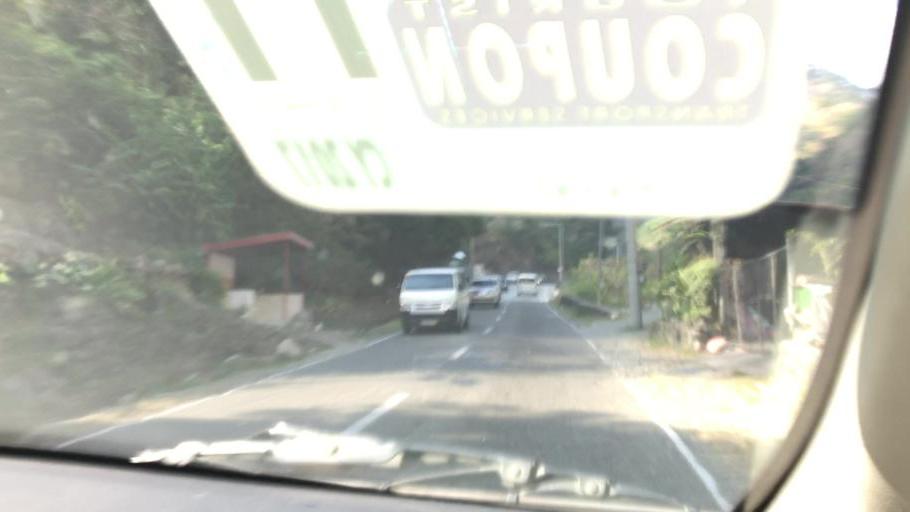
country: PH
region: Cordillera
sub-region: Province of Benguet
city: Tuba
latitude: 16.3229
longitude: 120.6152
